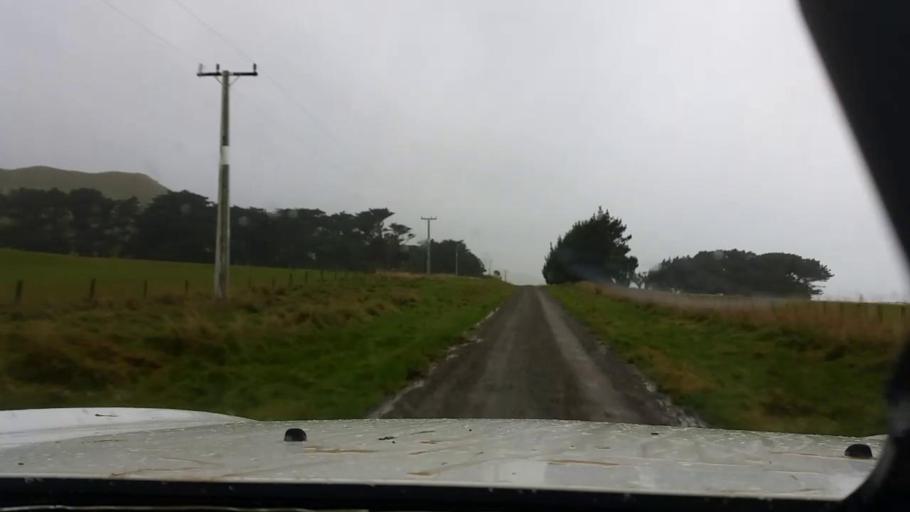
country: NZ
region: Wellington
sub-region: Masterton District
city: Masterton
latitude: -41.2588
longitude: 175.9006
